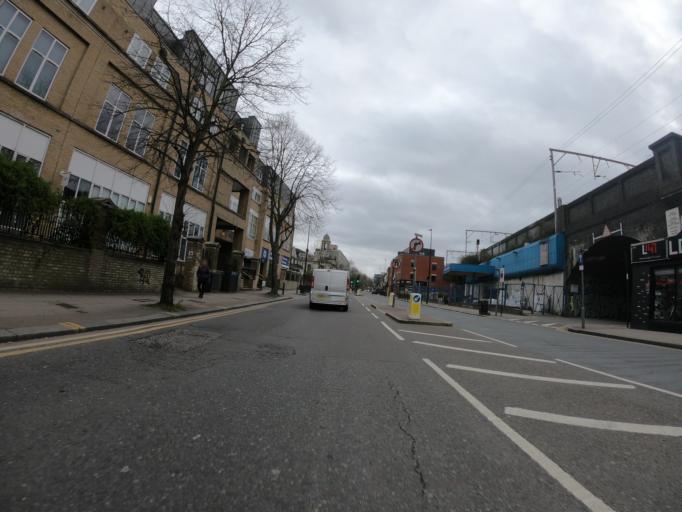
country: GB
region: England
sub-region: Greater London
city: Bethnal Green
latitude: 51.5313
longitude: -0.0566
